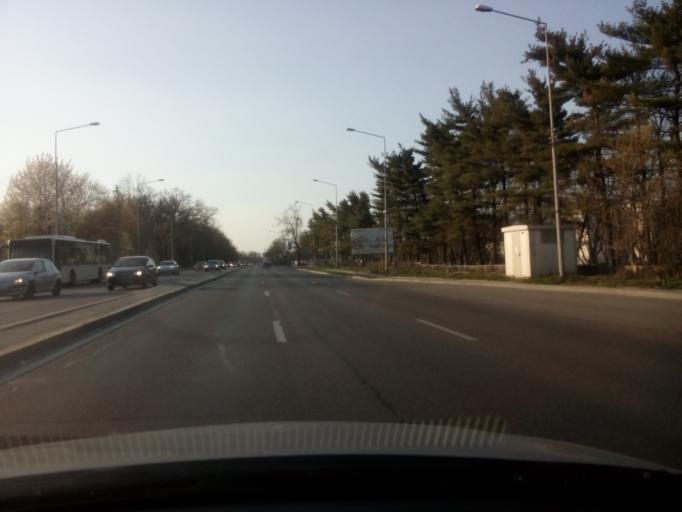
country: RO
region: Ilfov
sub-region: Comuna Otopeni
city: Otopeni
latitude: 44.5201
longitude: 26.0765
